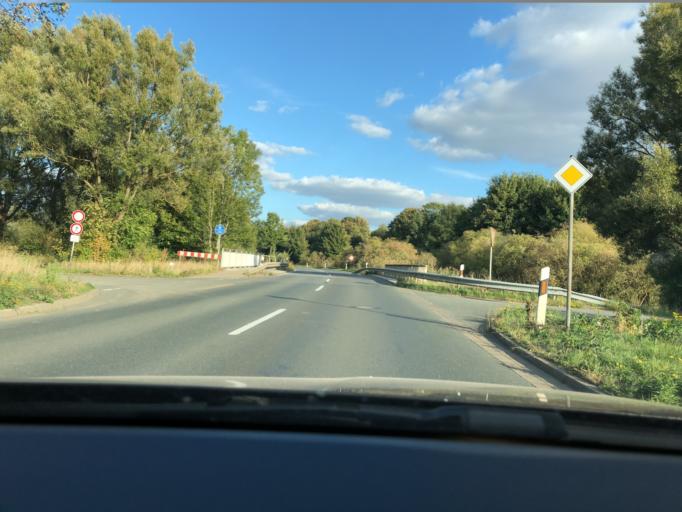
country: DE
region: Lower Saxony
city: Stuhr
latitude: 53.0204
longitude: 8.7759
